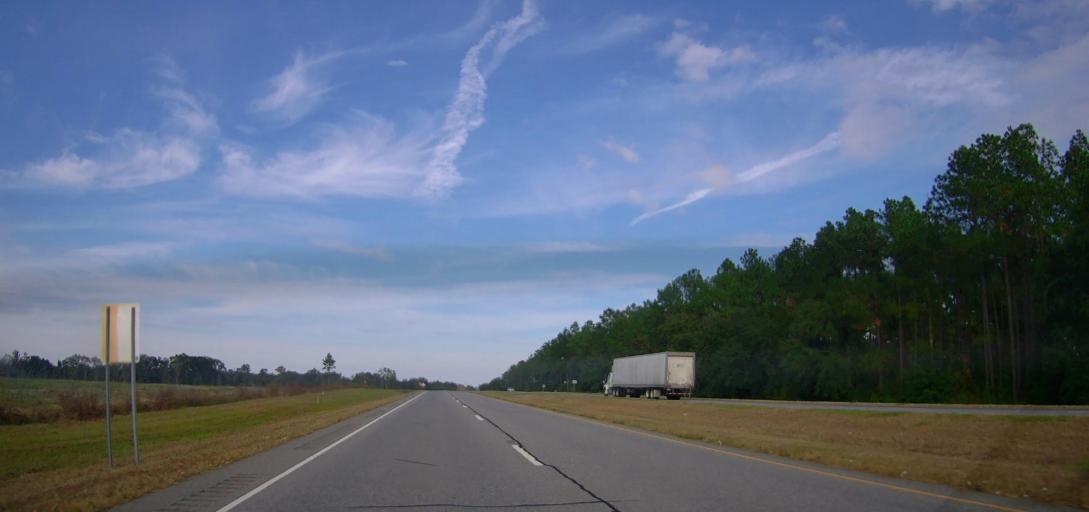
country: US
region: Georgia
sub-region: Mitchell County
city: Camilla
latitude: 31.2858
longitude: -84.1867
